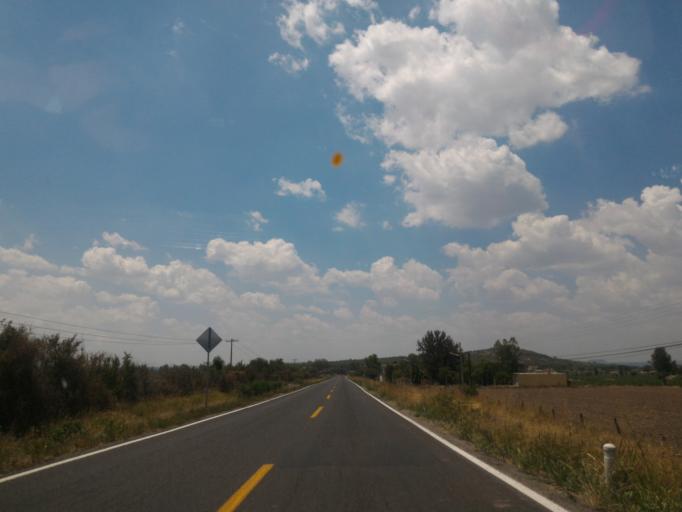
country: MX
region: Guanajuato
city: Ciudad Manuel Doblado
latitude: 20.7914
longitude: -101.9834
